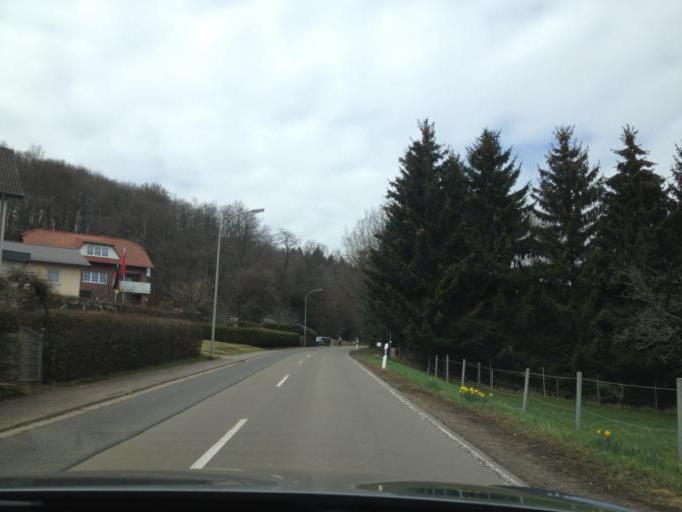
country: DE
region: Saarland
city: Freisen
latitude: 49.5580
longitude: 7.2445
